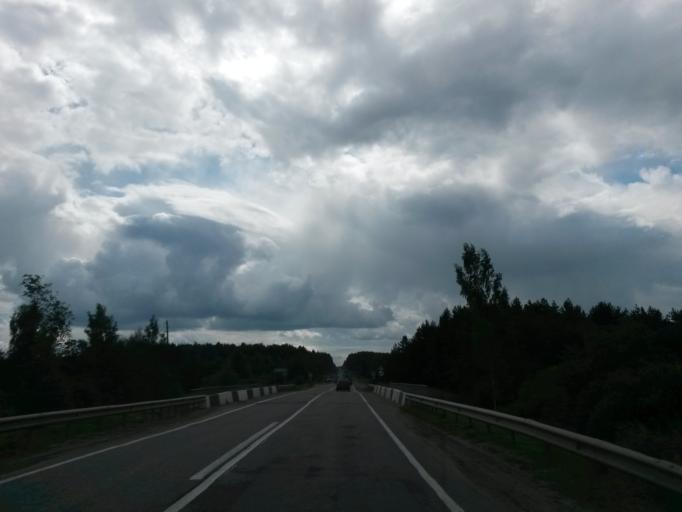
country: RU
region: Jaroslavl
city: Yaroslavl
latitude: 57.5111
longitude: 39.8974
